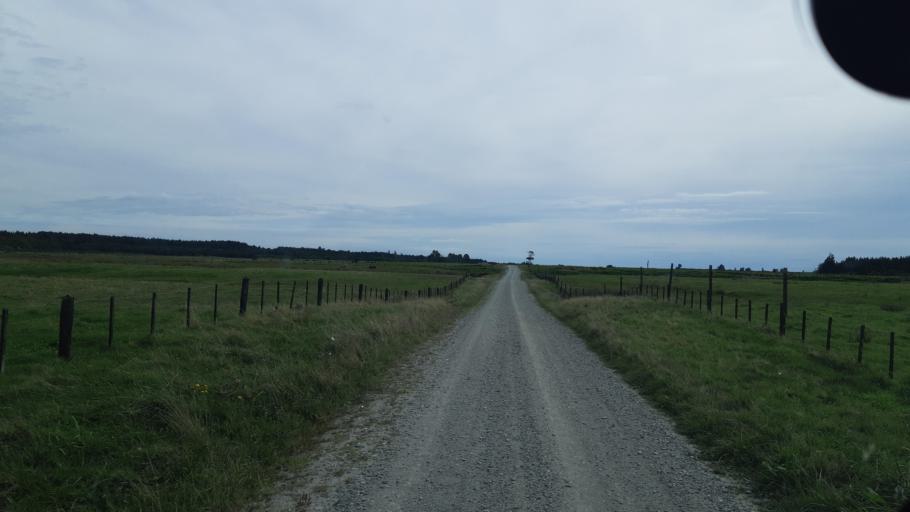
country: NZ
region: West Coast
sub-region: Westland District
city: Hokitika
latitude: -42.9724
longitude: 170.6769
